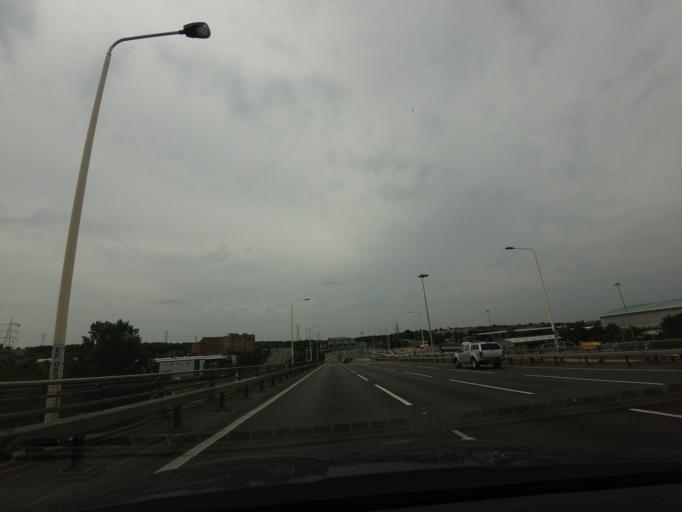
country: GB
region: England
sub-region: Kent
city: Stone
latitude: 51.4558
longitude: 0.2479
